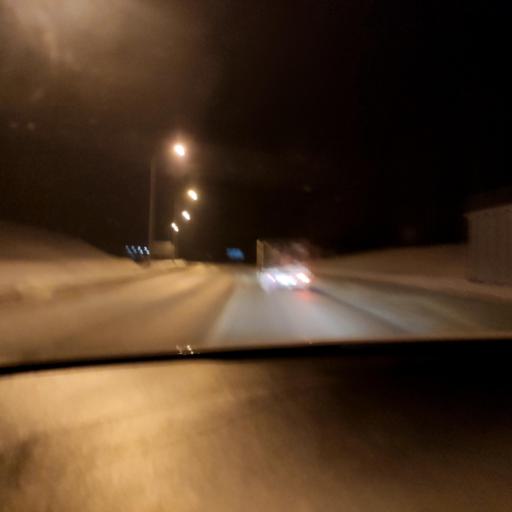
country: RU
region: Tatarstan
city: Aysha
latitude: 55.8758
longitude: 48.6595
